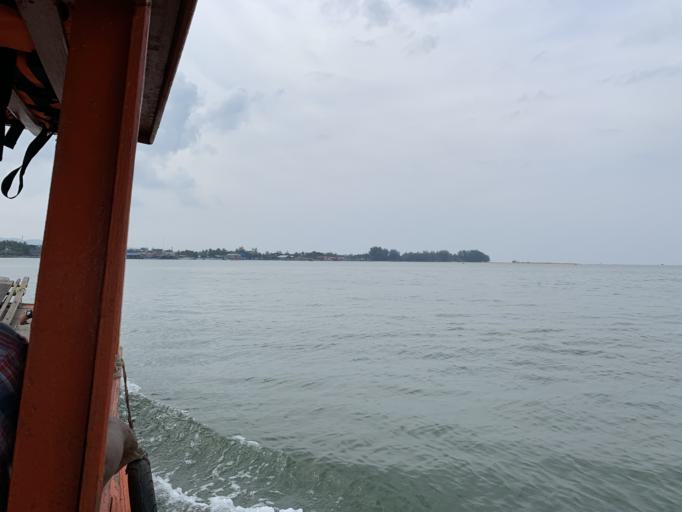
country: TH
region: Phangnga
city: Takua Pa
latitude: 8.8692
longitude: 98.2734
